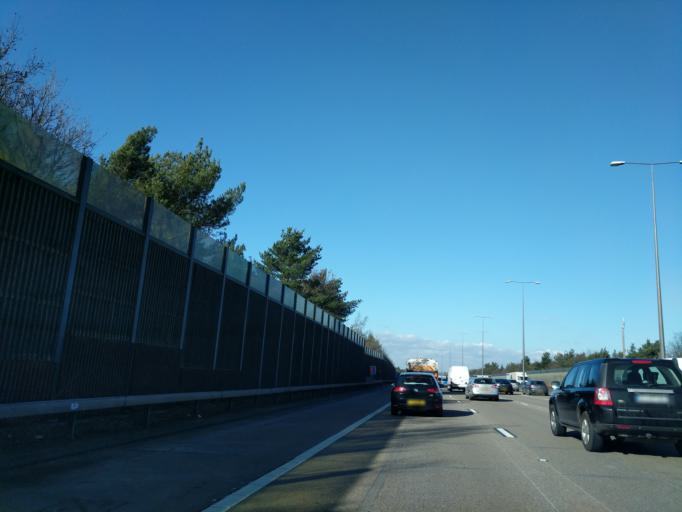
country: GB
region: England
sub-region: Surrey
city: Byfleet
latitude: 51.3508
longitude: -0.4879
